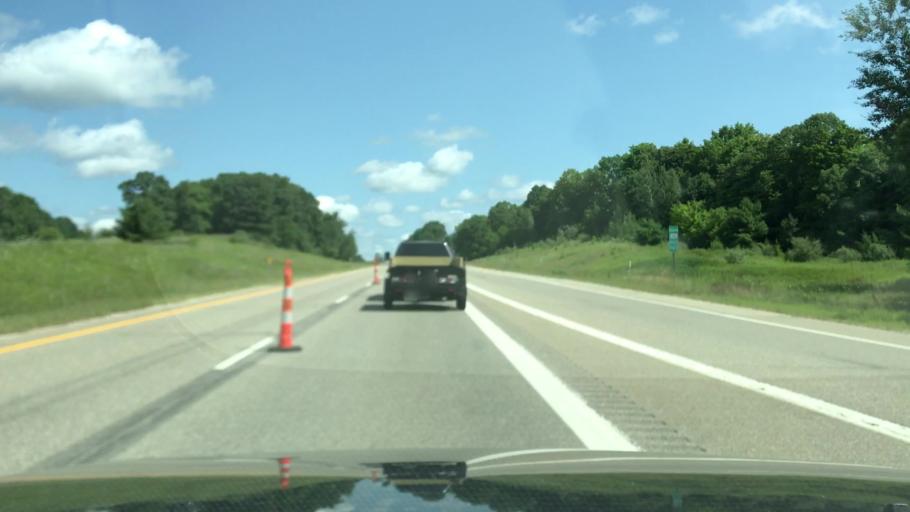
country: US
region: Michigan
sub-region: Mecosta County
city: Big Rapids
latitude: 43.7471
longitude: -85.5295
